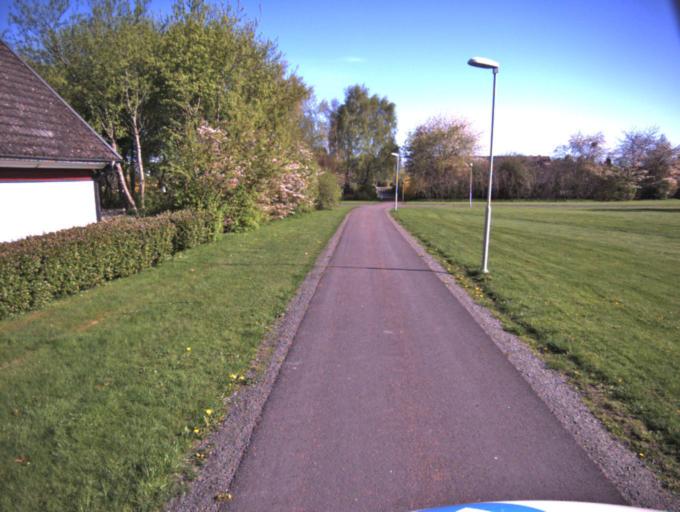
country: SE
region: Skane
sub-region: Kristianstads Kommun
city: Kristianstad
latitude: 56.0133
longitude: 14.0959
